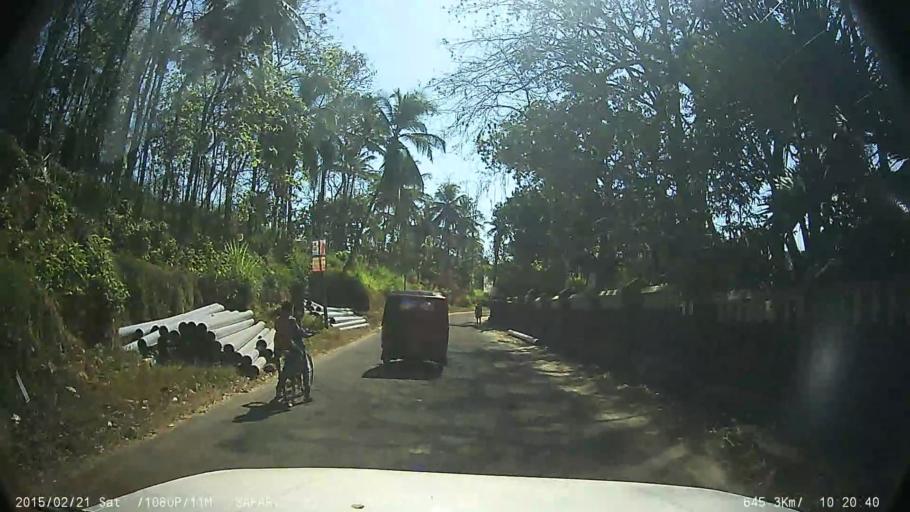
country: IN
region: Kerala
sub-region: Kottayam
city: Palackattumala
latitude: 9.8696
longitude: 76.6641
